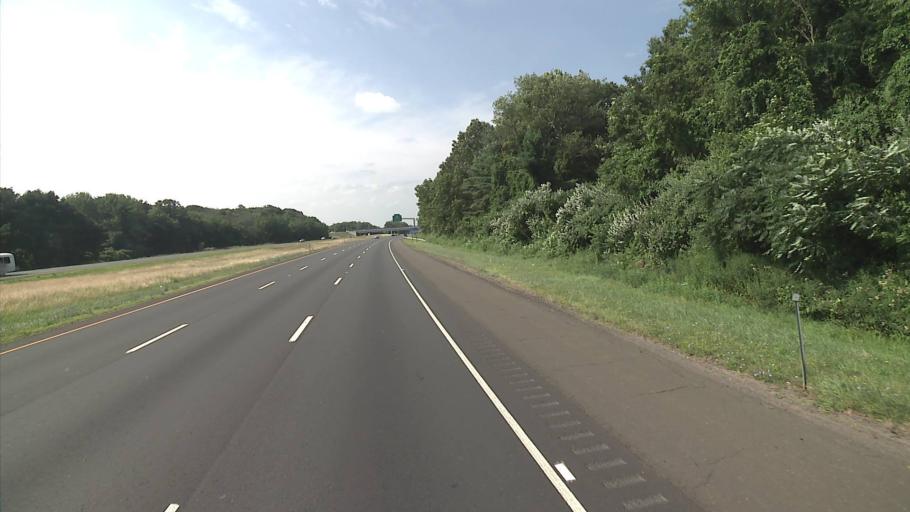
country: US
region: Connecticut
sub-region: New Haven County
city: Wallingford
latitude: 41.4860
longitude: -72.7681
